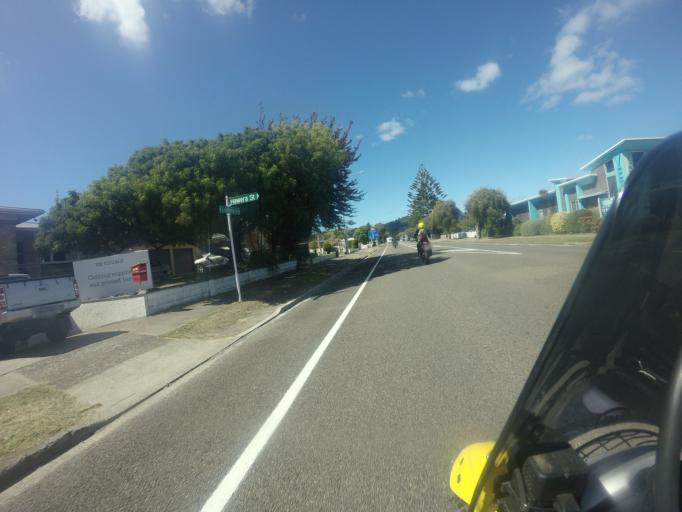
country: NZ
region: Bay of Plenty
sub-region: Whakatane District
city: Whakatane
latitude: -37.9584
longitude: 176.9793
